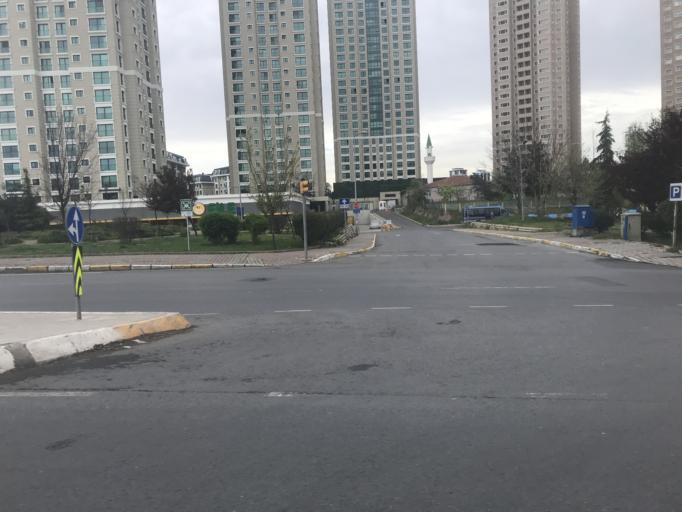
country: TR
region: Istanbul
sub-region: Atasehir
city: Atasehir
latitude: 40.9880
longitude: 29.1441
